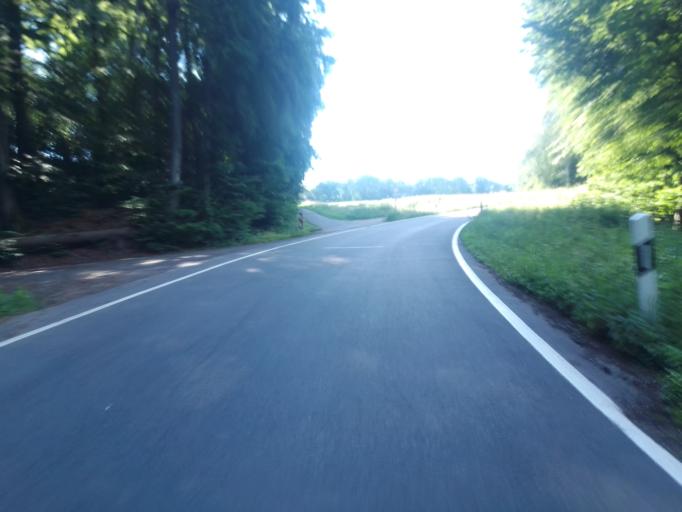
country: DE
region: Bavaria
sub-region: Regierungsbezirk Unterfranken
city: Hasloch
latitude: 49.7977
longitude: 9.4846
